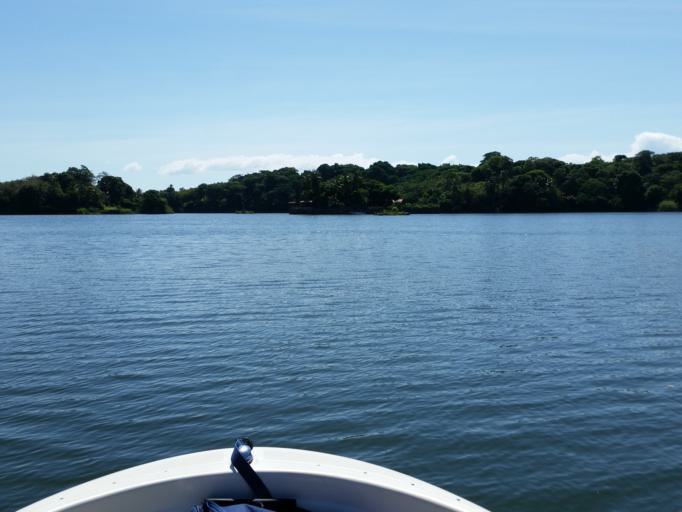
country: NI
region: Granada
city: Granada
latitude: 11.8798
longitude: -85.8966
